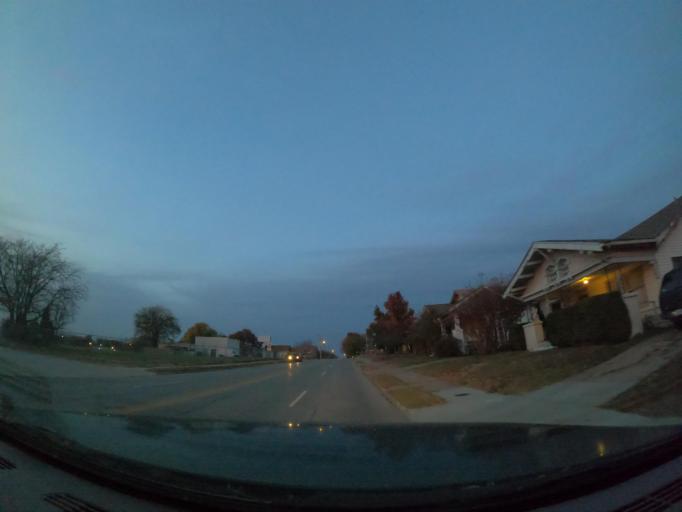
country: US
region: Oklahoma
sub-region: Tulsa County
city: Tulsa
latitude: 36.1613
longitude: -95.9671
